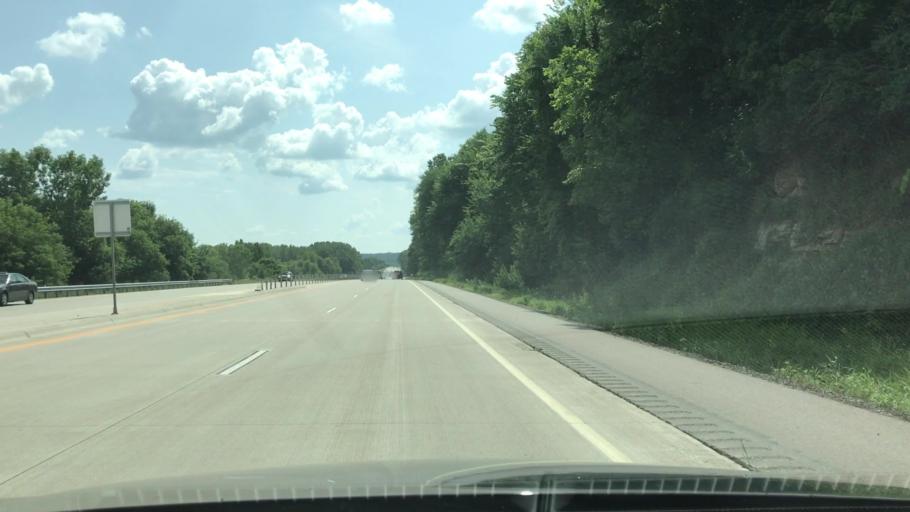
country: US
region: Minnesota
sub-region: Nicollet County
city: Saint Peter
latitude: 44.2882
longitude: -94.0018
